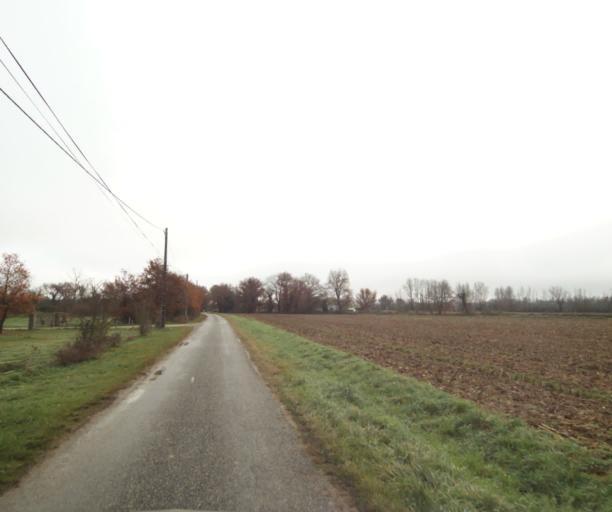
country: FR
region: Midi-Pyrenees
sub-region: Departement de la Haute-Garonne
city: Villemur-sur-Tarn
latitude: 43.8760
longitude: 1.4698
